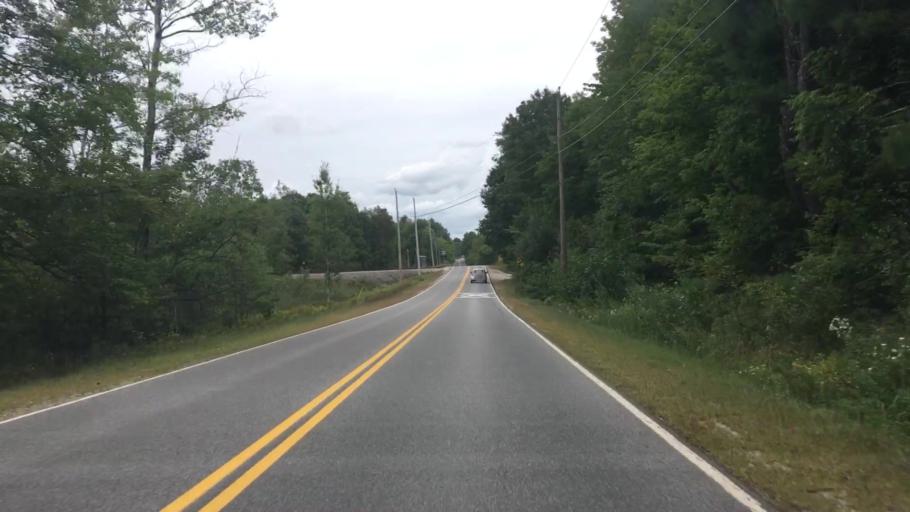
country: US
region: Maine
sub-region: Cumberland County
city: Yarmouth
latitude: 43.8587
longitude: -70.2178
